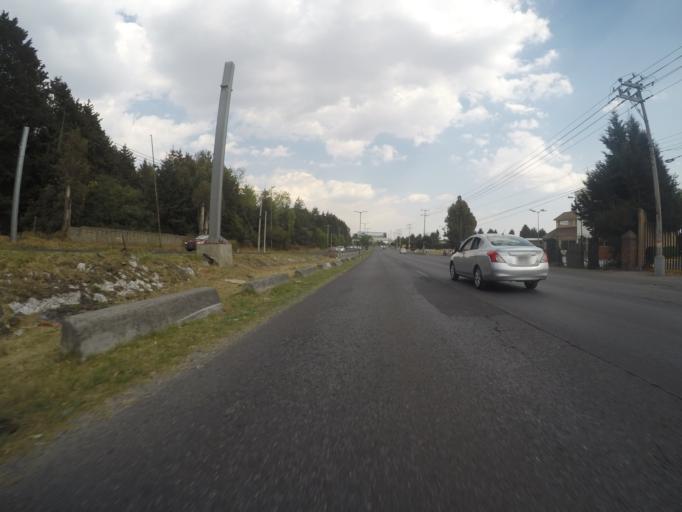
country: MX
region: Morelos
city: Metepec
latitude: 19.2442
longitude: -99.6043
